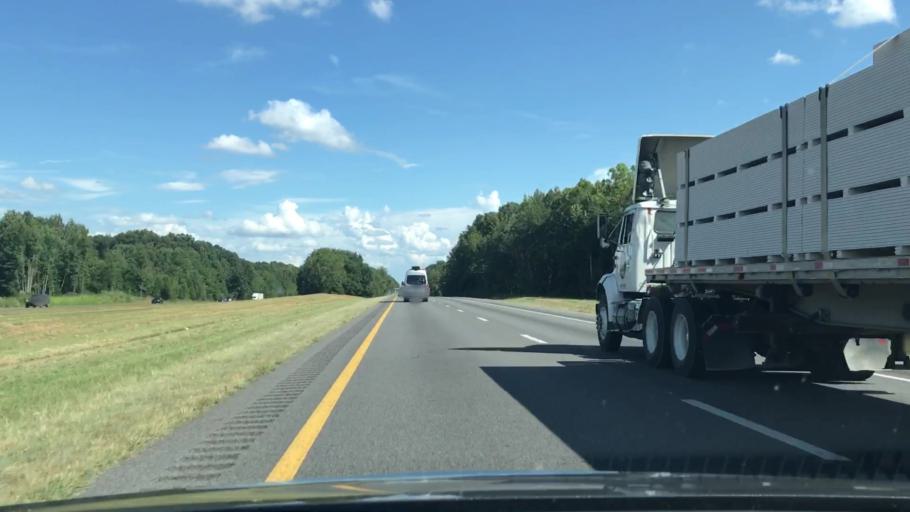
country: US
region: Kentucky
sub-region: Todd County
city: Guthrie
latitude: 36.5049
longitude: -87.1926
